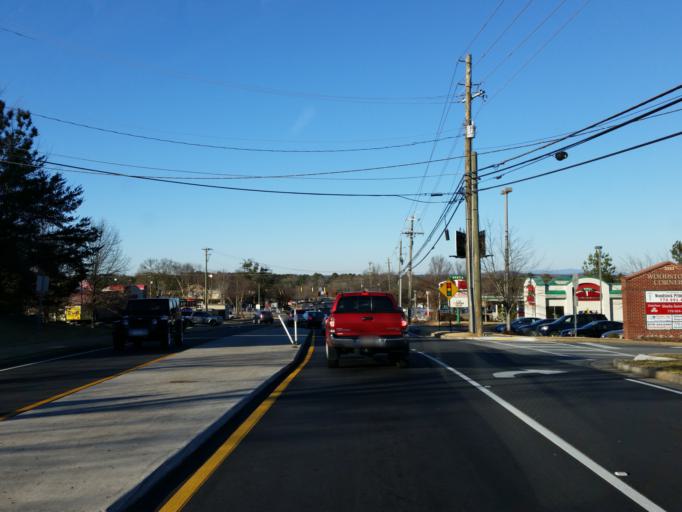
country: US
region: Georgia
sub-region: Cherokee County
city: Woodstock
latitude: 34.0860
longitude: -84.4845
